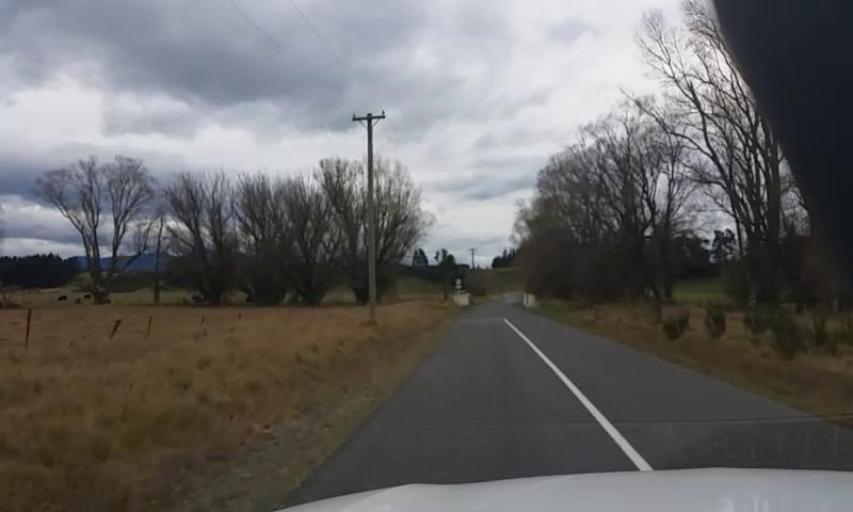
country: NZ
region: Canterbury
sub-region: Waimakariri District
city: Kaiapoi
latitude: -43.3031
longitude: 172.4379
